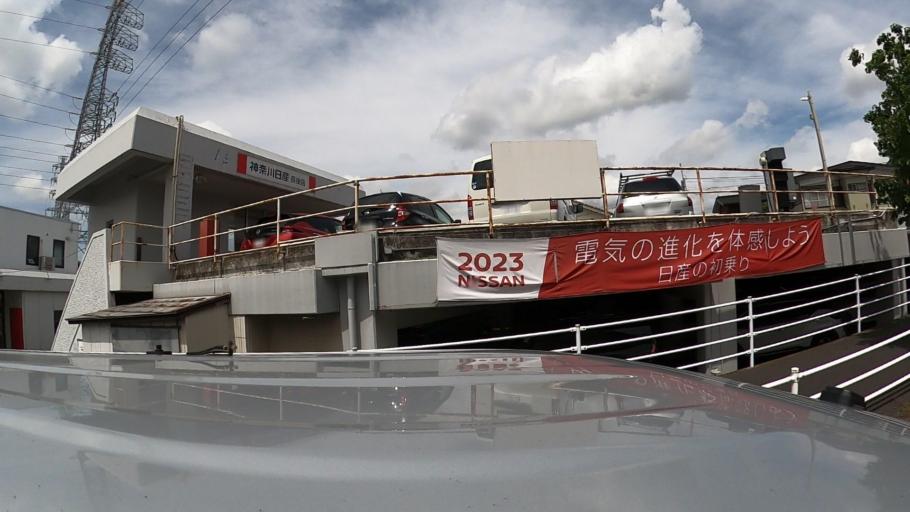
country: JP
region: Kanagawa
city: Fujisawa
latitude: 35.4127
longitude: 139.4697
